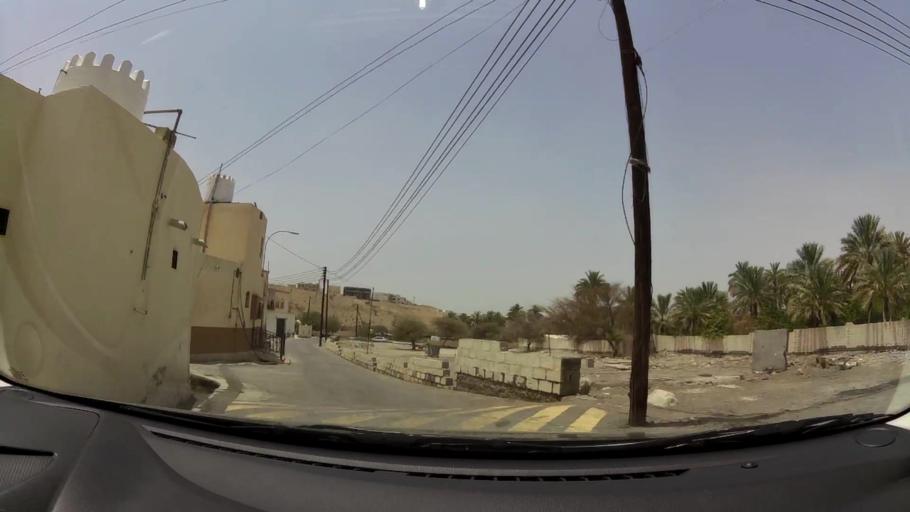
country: OM
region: Muhafazat Masqat
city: Bawshar
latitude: 23.5318
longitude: 58.3906
